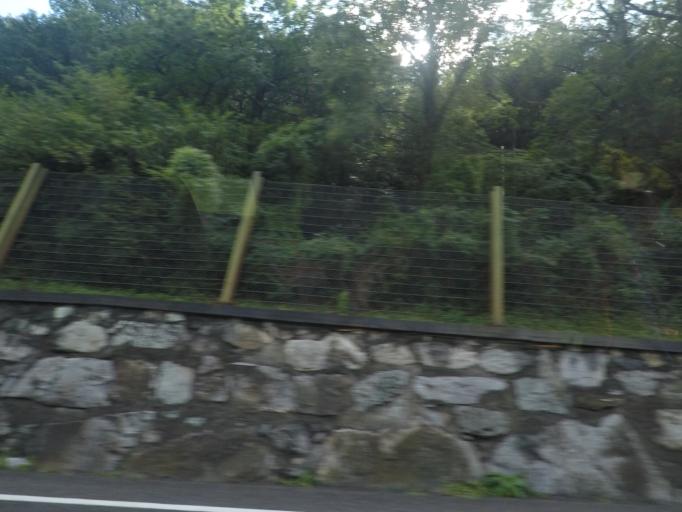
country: IT
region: Aosta Valley
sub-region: Valle d'Aosta
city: Chatillon
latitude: 45.7687
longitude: 7.6004
